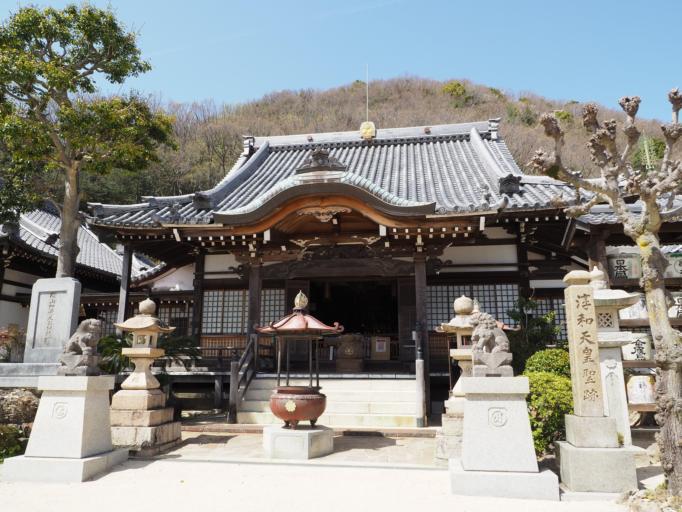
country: JP
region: Hyogo
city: Takarazuka
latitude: 34.7730
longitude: 135.3299
